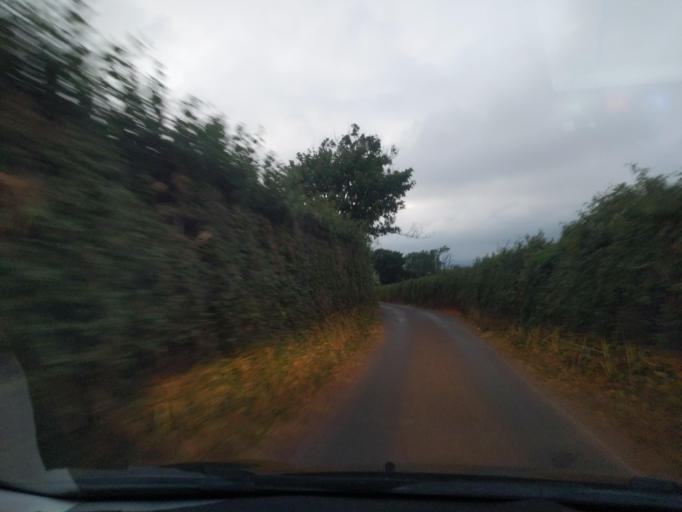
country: GB
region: England
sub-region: Devon
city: Marldon
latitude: 50.4742
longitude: -3.6151
